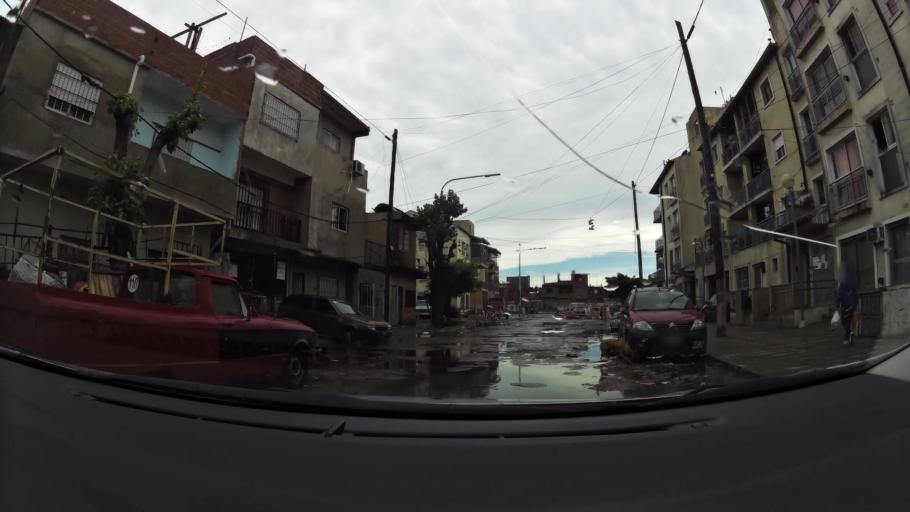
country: AR
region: Buenos Aires F.D.
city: Villa Lugano
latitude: -34.6596
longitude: -58.4553
